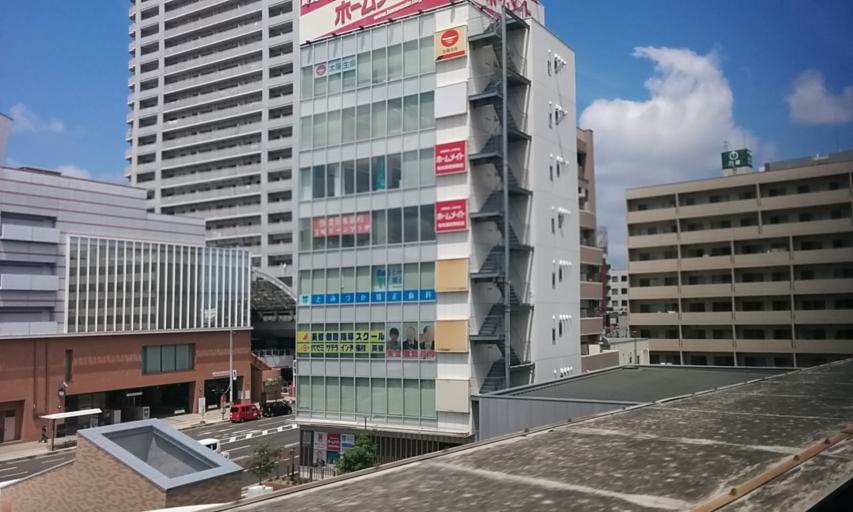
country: JP
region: Miyagi
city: Sendai
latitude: 38.2274
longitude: 140.8856
